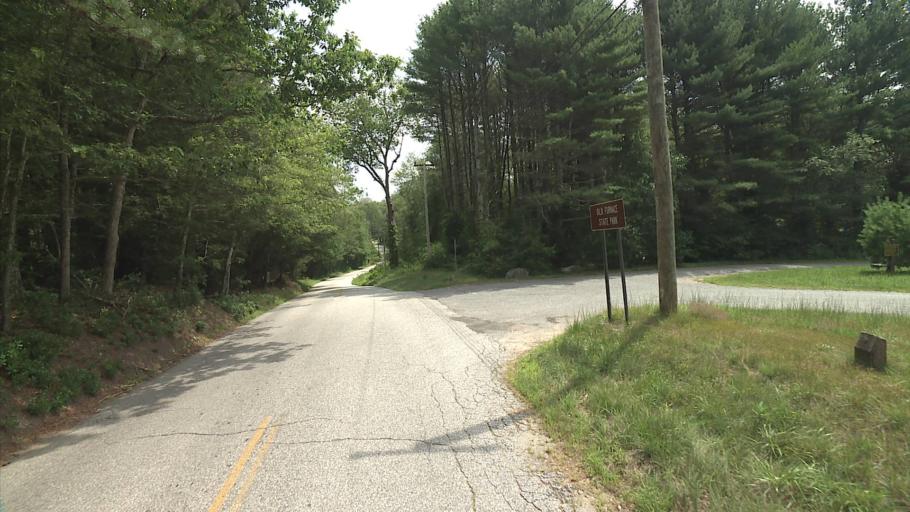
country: US
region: Connecticut
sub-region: Windham County
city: Danielson
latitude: 41.7890
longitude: -71.8656
